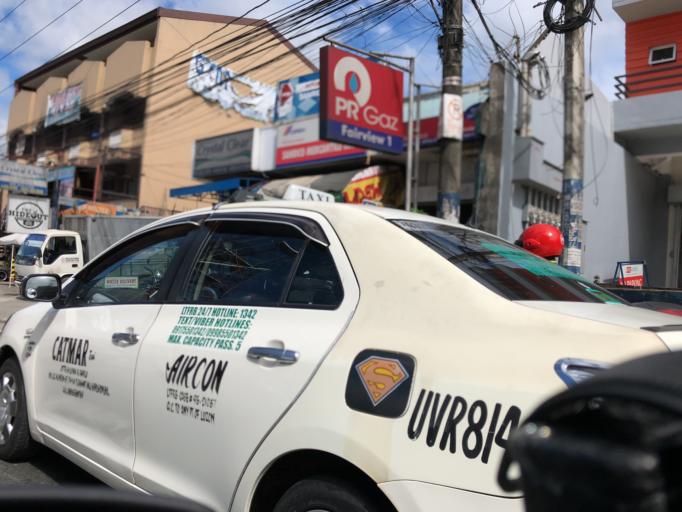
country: PH
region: Calabarzon
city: Bagong Pagasa
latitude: 14.7170
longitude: 121.0612
